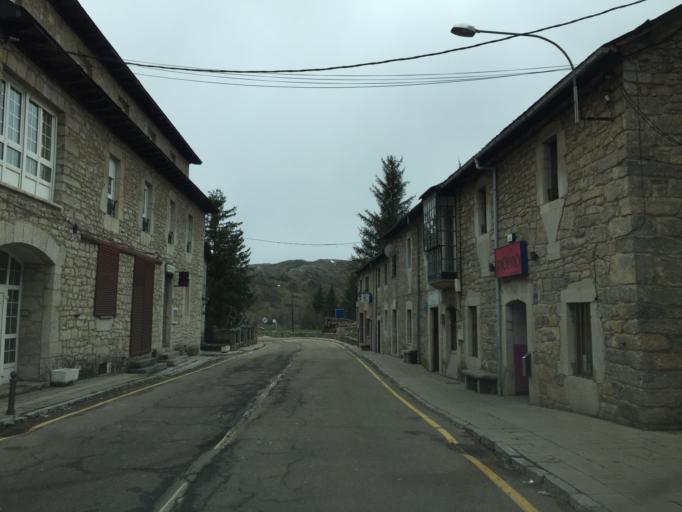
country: ES
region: Castille and Leon
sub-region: Provincia de Leon
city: San Emiliano
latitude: 42.9711
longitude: -6.0008
